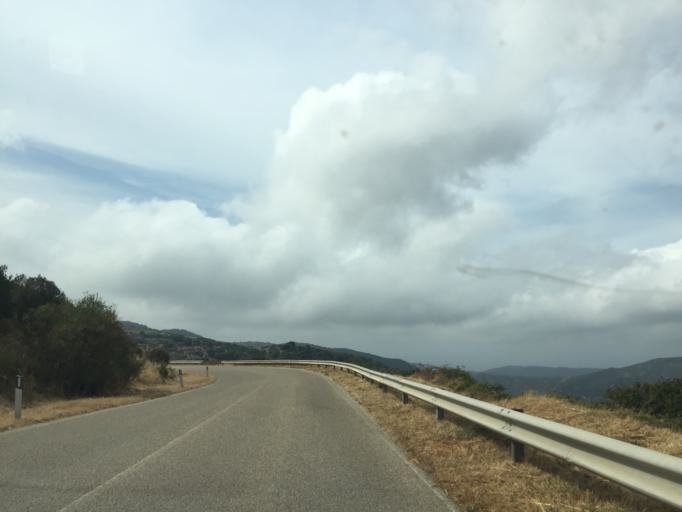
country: IT
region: Sardinia
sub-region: Provincia di Olbia-Tempio
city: Trinita d'Agultu
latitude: 40.9757
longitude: 8.9464
